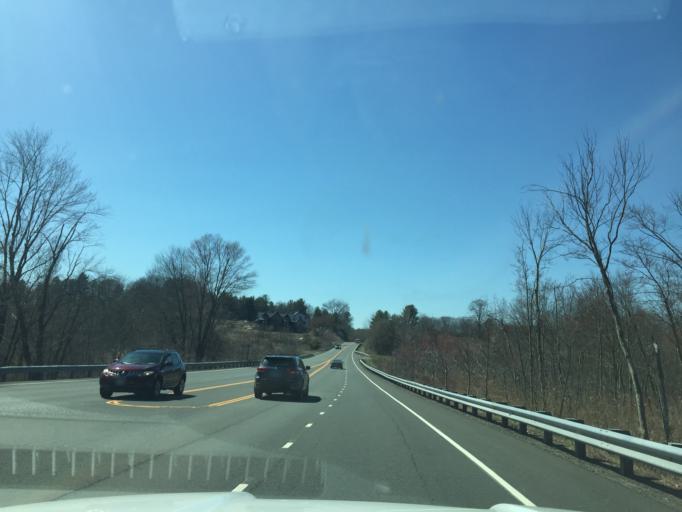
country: US
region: Connecticut
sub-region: Hartford County
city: Tariffville
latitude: 41.9472
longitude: -72.7408
